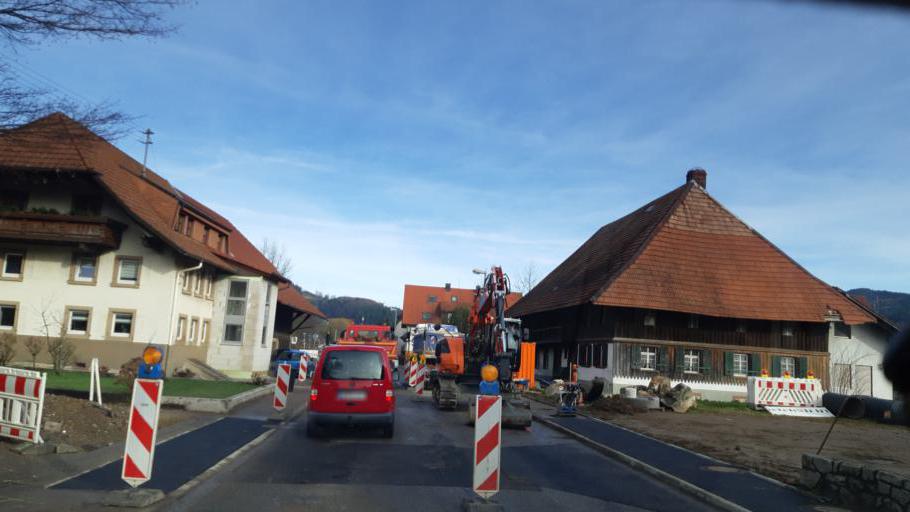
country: DE
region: Baden-Wuerttemberg
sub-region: Freiburg Region
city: Gutach im Breisgau
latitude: 48.1437
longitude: 8.0240
